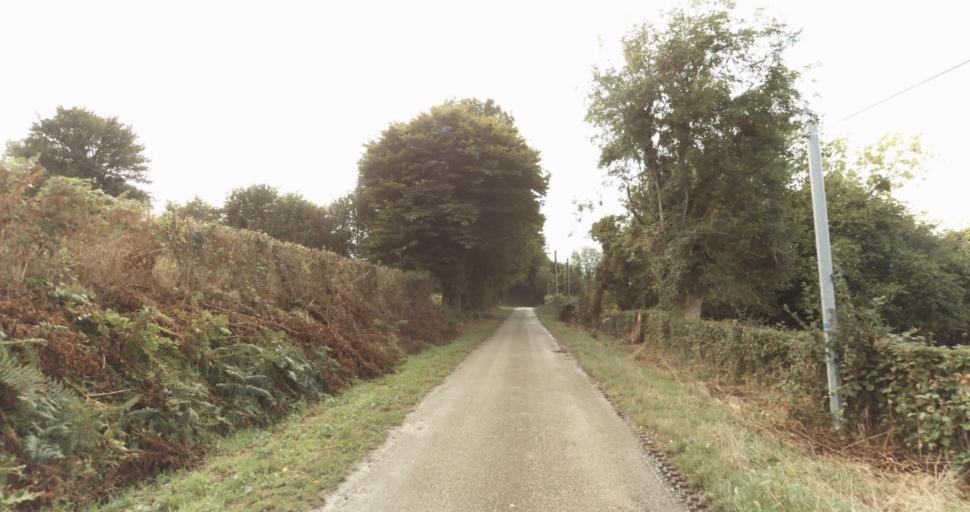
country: FR
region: Lower Normandy
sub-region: Departement de l'Orne
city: Vimoutiers
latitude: 48.8583
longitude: 0.1509
